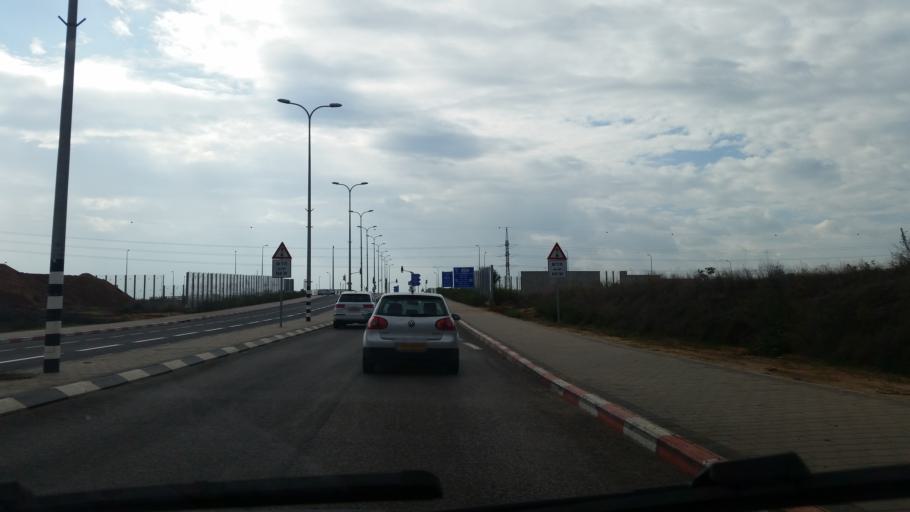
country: IL
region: Central District
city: Ra'anana
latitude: 32.1740
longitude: 34.8688
